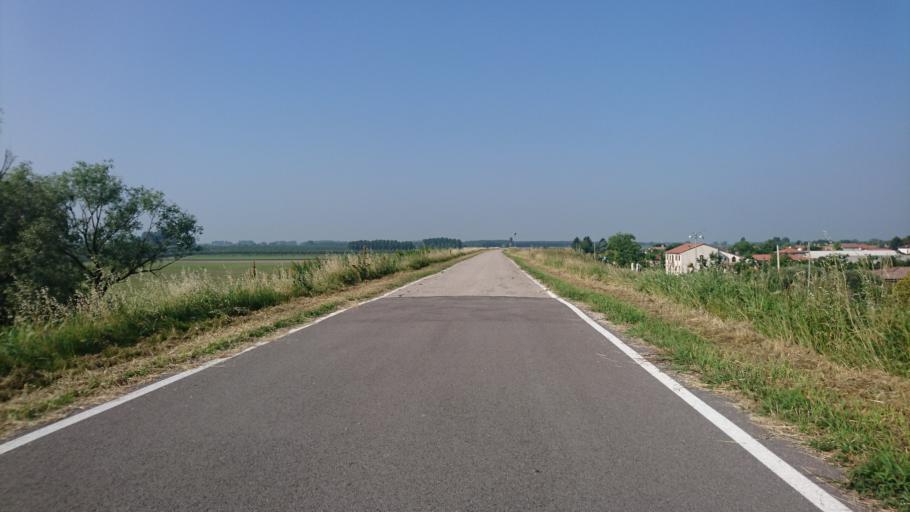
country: IT
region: Veneto
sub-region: Provincia di Rovigo
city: Bergantino
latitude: 45.0581
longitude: 11.2522
